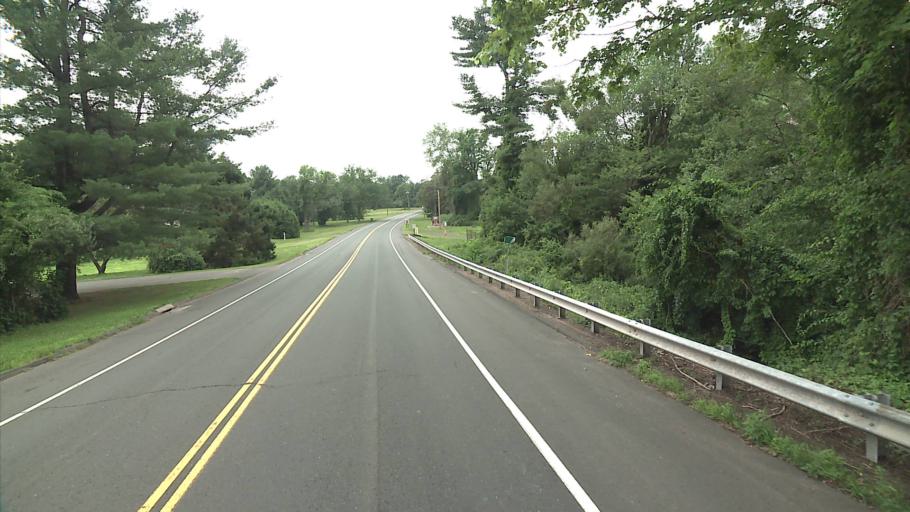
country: US
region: Connecticut
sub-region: Middlesex County
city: Cromwell
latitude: 41.6360
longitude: -72.6488
